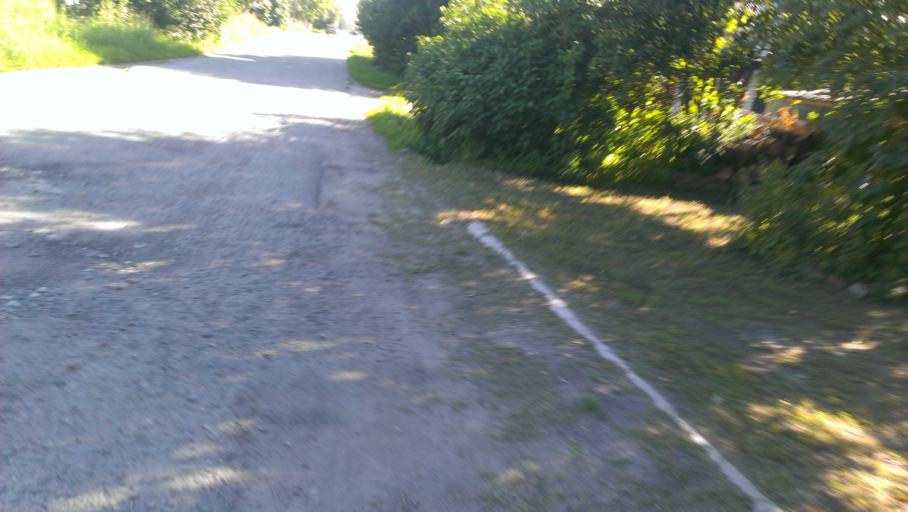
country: RU
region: Altai Krai
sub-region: Gorod Barnaulskiy
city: Barnaul
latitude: 53.3558
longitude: 83.7400
